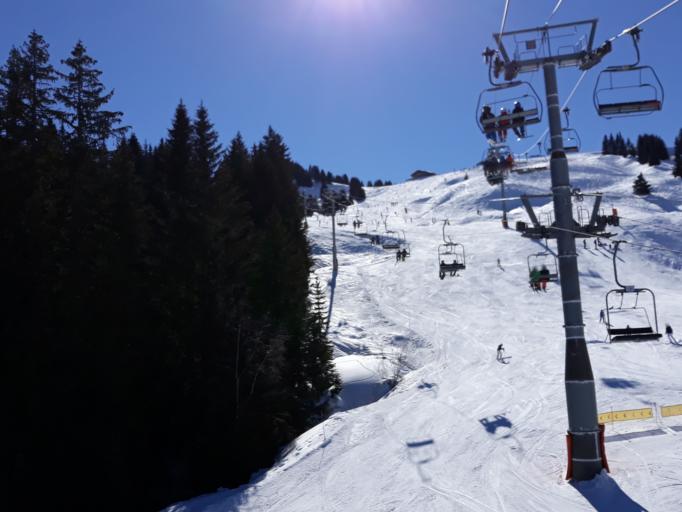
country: FR
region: Rhone-Alpes
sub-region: Departement de la Haute-Savoie
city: Araches-la-Frasse
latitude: 46.0474
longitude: 6.6691
